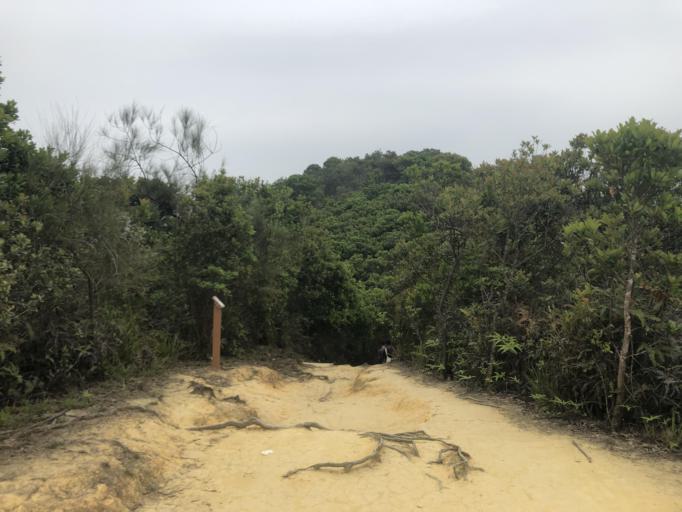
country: HK
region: Sha Tin
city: Sha Tin
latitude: 22.3817
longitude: 114.1540
